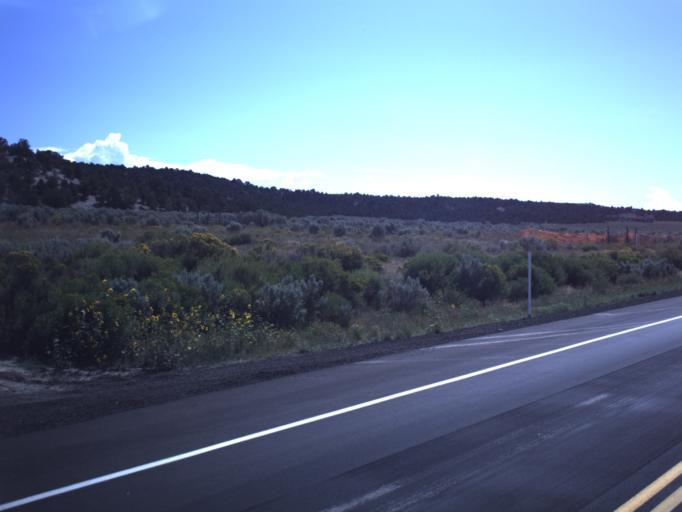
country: US
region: Utah
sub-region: Utah County
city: Genola
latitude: 39.9704
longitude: -112.2562
